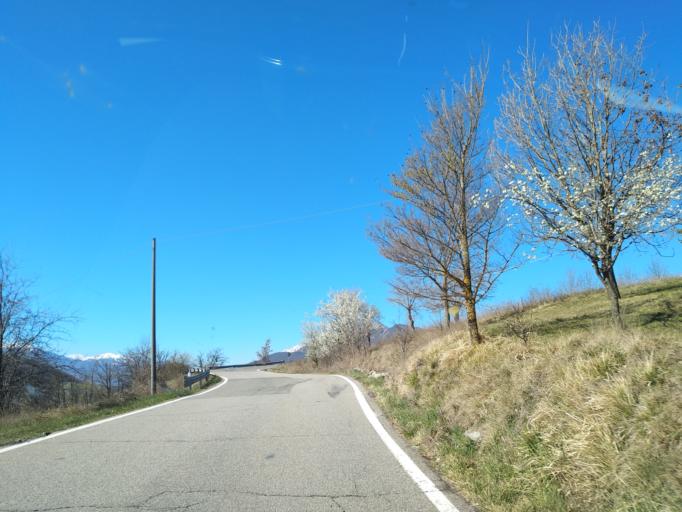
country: IT
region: Emilia-Romagna
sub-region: Provincia di Reggio Emilia
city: Castelnovo ne'Monti
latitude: 44.4070
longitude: 10.3980
